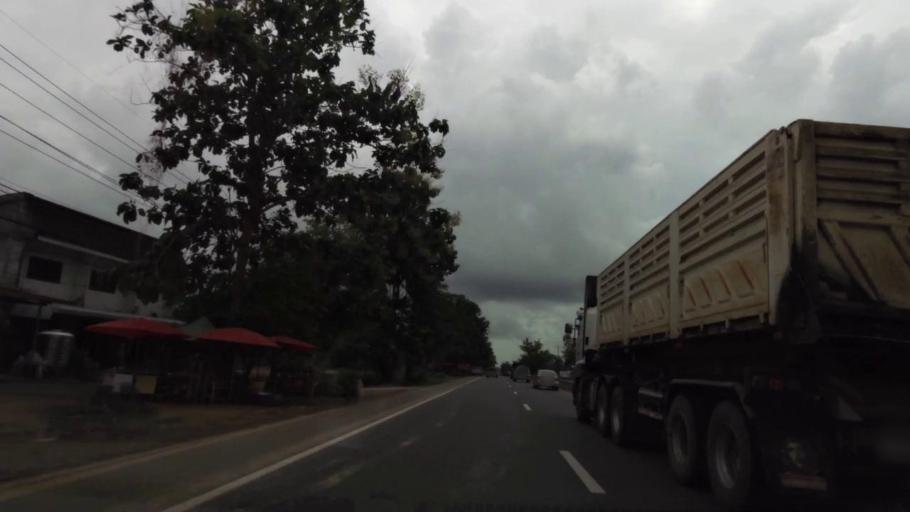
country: TH
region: Chanthaburi
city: Chanthaburi
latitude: 12.6586
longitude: 102.0623
